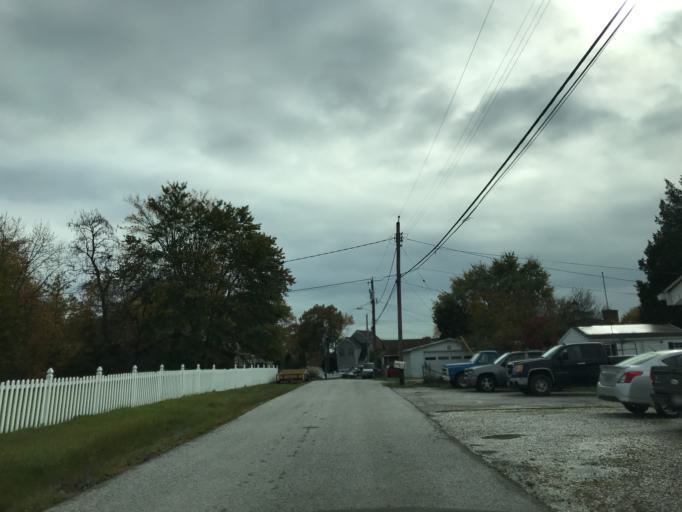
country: US
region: Maryland
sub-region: Baltimore County
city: Bowleys Quarters
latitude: 39.3200
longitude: -76.3998
